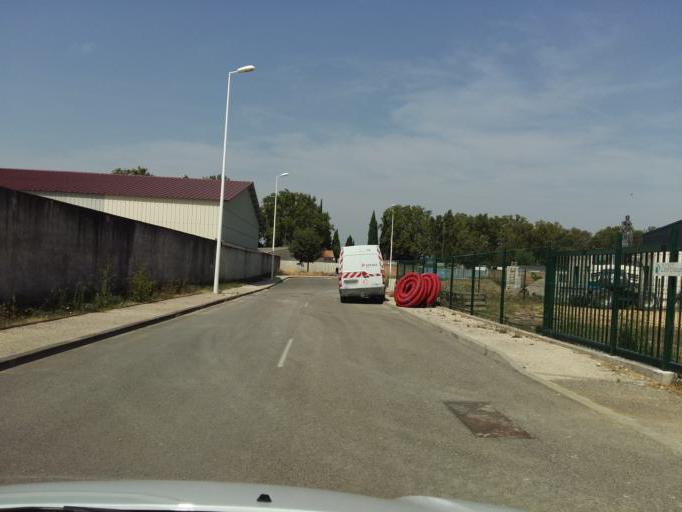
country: FR
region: Provence-Alpes-Cote d'Azur
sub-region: Departement du Vaucluse
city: Mondragon
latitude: 44.2624
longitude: 4.7063
